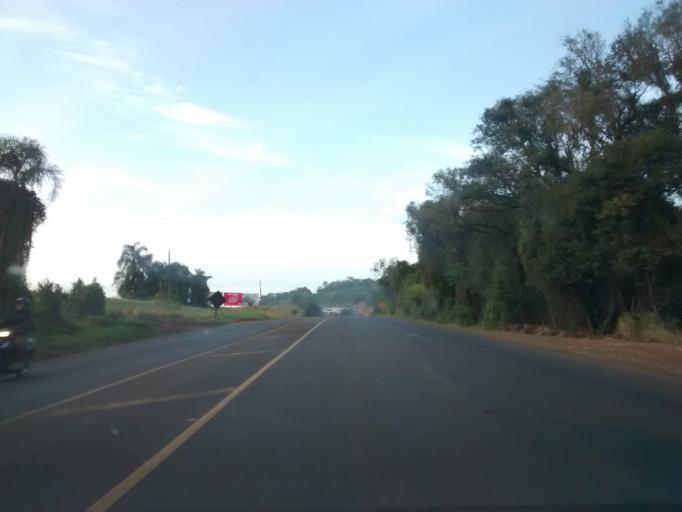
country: BR
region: Parana
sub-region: Francisco Beltrao
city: Francisco Beltrao
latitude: -26.1262
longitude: -53.0409
